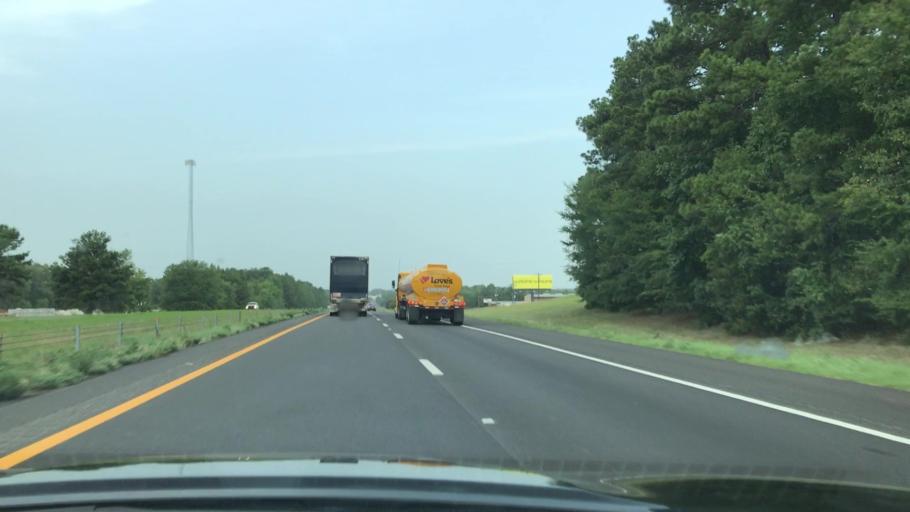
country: US
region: Texas
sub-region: Harrison County
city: Hallsville
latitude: 32.4645
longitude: -94.6376
